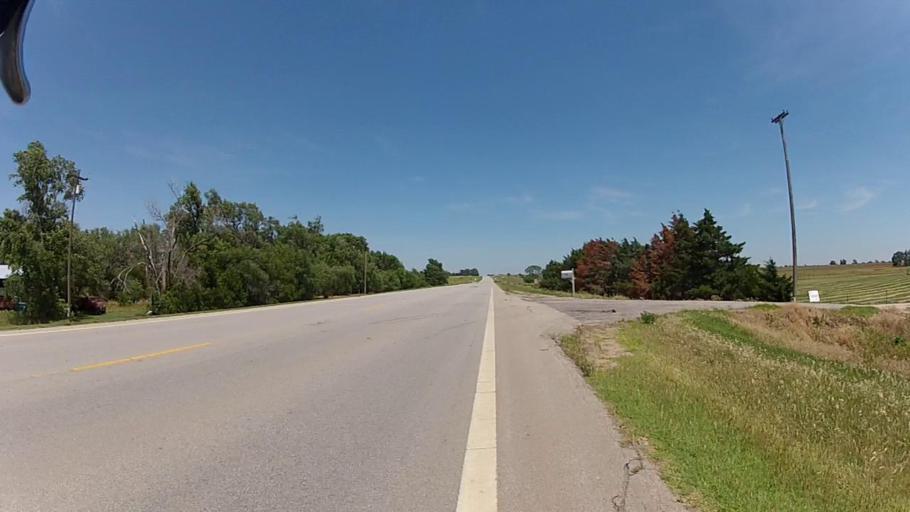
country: US
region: Kansas
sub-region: Harper County
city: Harper
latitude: 37.2386
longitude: -98.1202
